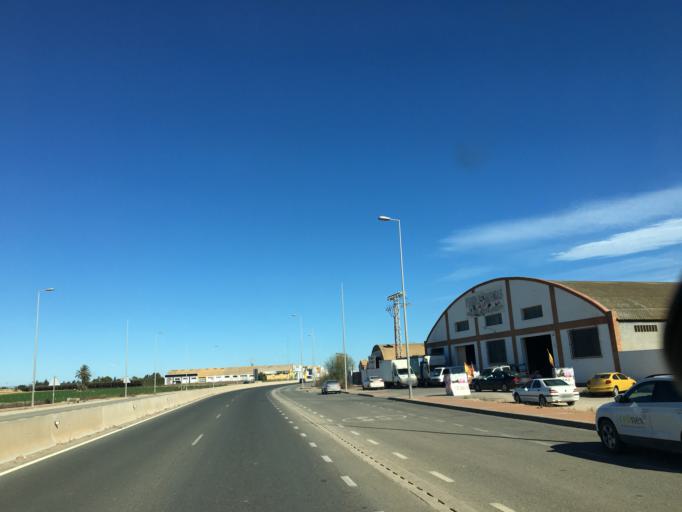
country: ES
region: Murcia
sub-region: Murcia
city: Cartagena
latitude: 37.6448
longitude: -0.9860
